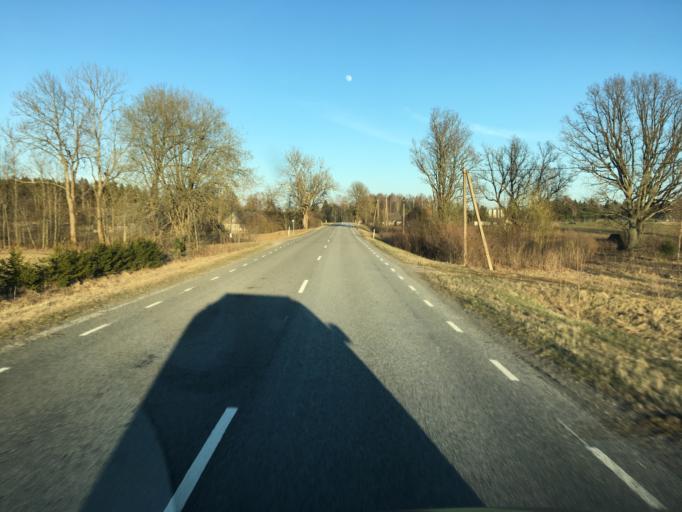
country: EE
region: Raplamaa
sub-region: Rapla vald
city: Rapla
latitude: 59.0767
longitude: 24.8674
